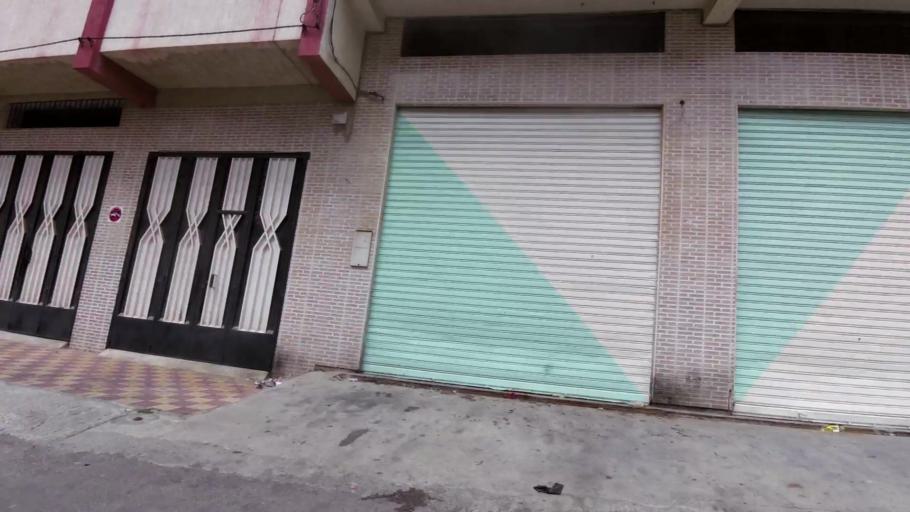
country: MA
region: Tanger-Tetouan
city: Tetouan
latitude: 35.5771
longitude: -5.3619
